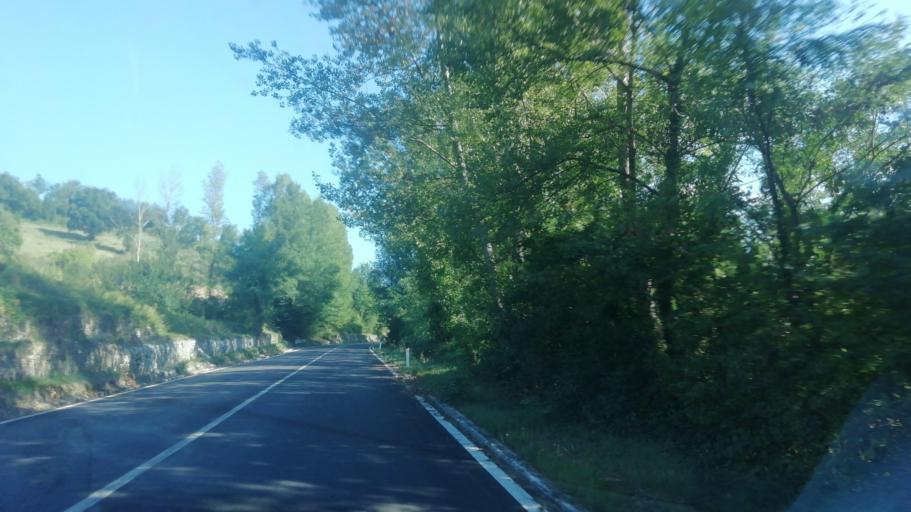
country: IT
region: The Marches
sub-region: Provincia di Pesaro e Urbino
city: Frontone
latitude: 43.5397
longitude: 12.7456
